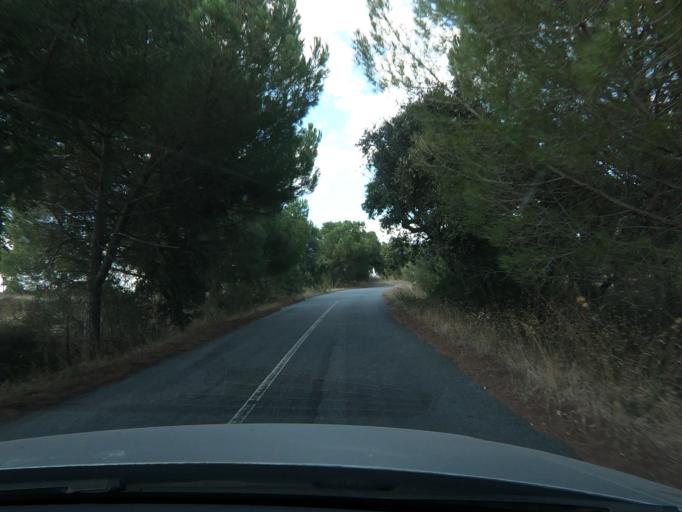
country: PT
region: Setubal
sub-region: Alcacer do Sal
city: Alcacer do Sal
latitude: 38.2572
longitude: -8.3568
